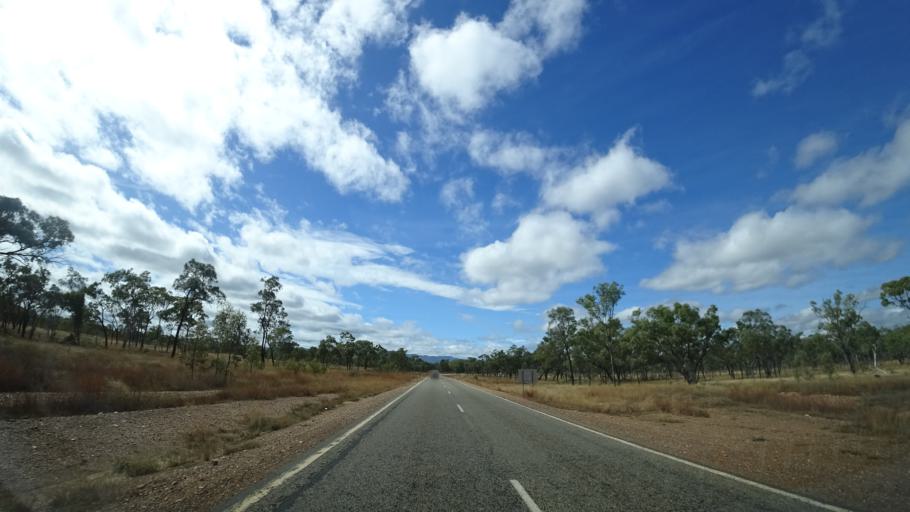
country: AU
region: Queensland
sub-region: Cairns
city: Port Douglas
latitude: -16.4970
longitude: 144.9916
